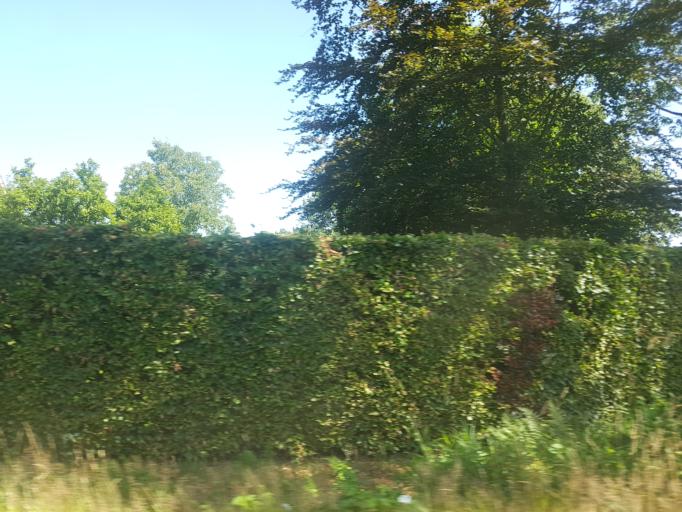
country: NL
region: North Brabant
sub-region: Gemeente Boxtel
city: Boxtel
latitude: 51.5795
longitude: 5.2884
